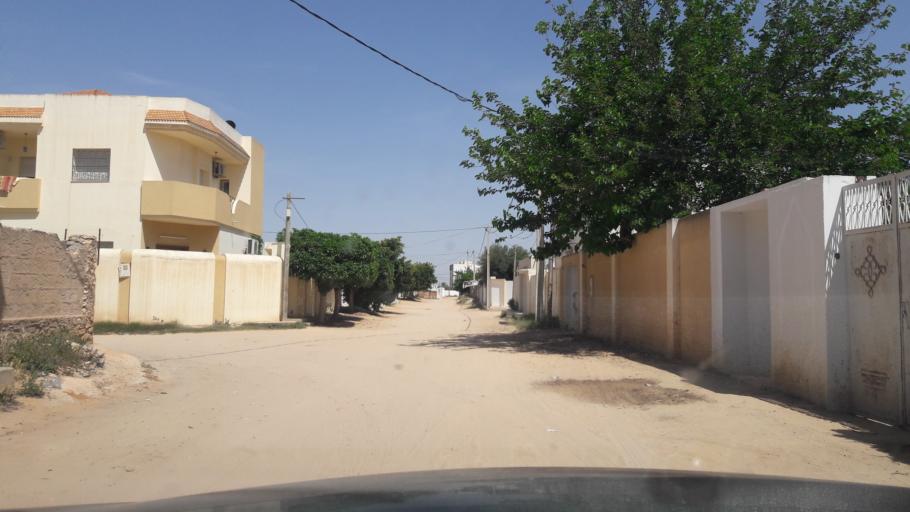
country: TN
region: Safaqis
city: Al Qarmadah
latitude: 34.7932
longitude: 10.7578
